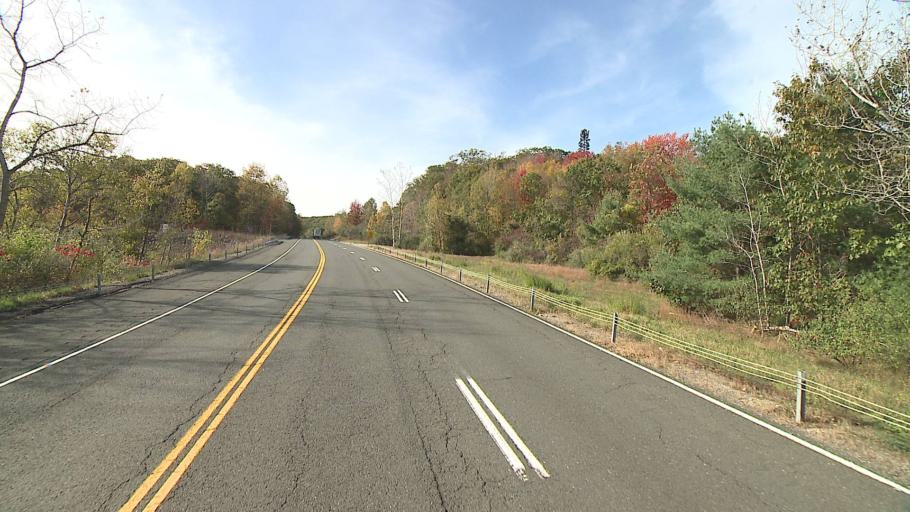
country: US
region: Connecticut
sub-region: Litchfield County
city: Winsted
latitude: 41.9379
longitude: -73.0936
